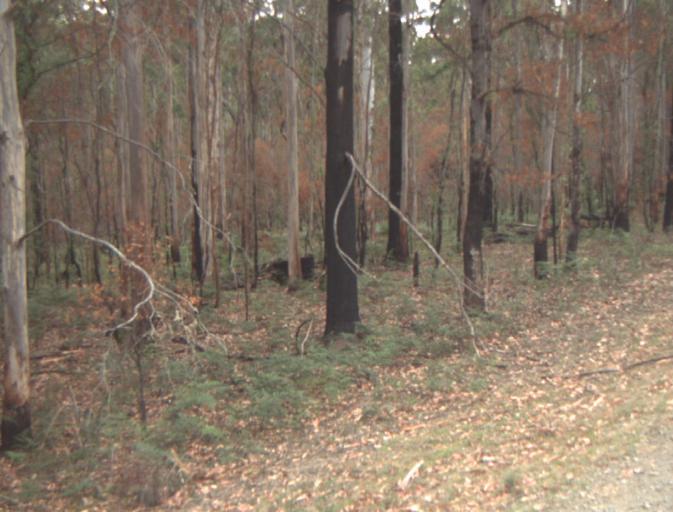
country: AU
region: Tasmania
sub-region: Dorset
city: Scottsdale
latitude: -41.4325
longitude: 147.5149
